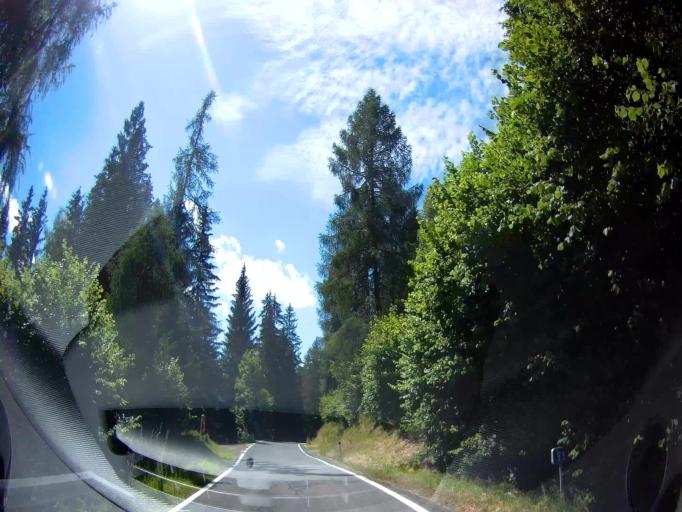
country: AT
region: Carinthia
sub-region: Politischer Bezirk Sankt Veit an der Glan
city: Glodnitz
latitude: 46.9155
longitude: 14.0786
